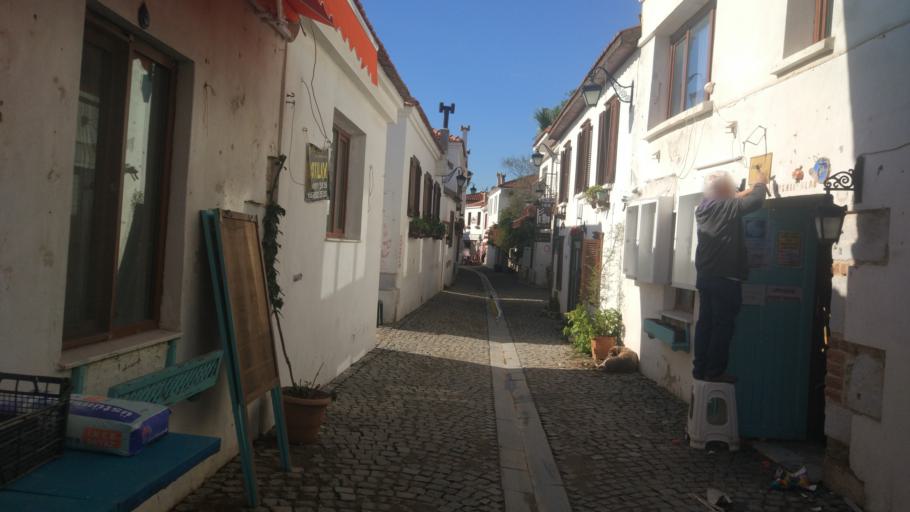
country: TR
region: Izmir
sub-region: Seferihisar
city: Seferhisar
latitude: 38.1947
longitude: 26.7857
